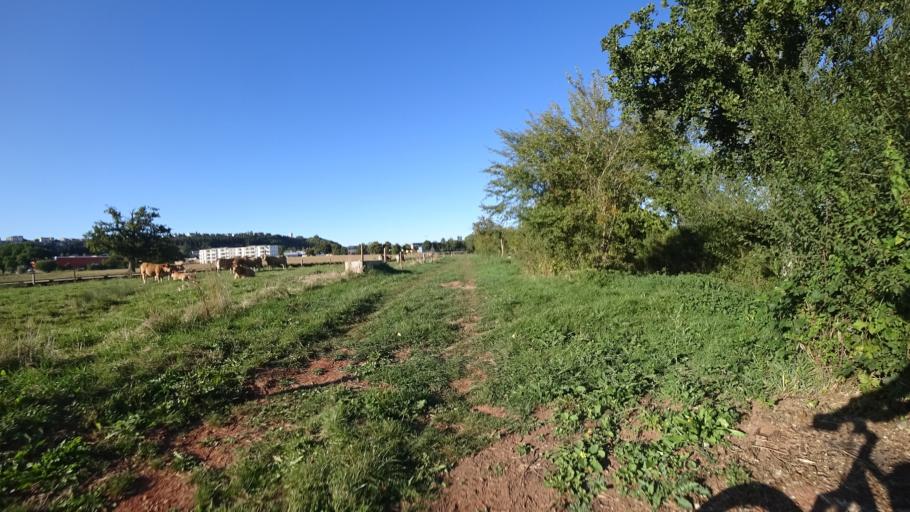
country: FR
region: Midi-Pyrenees
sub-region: Departement de l'Aveyron
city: Rodez
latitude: 44.3694
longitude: 2.5803
